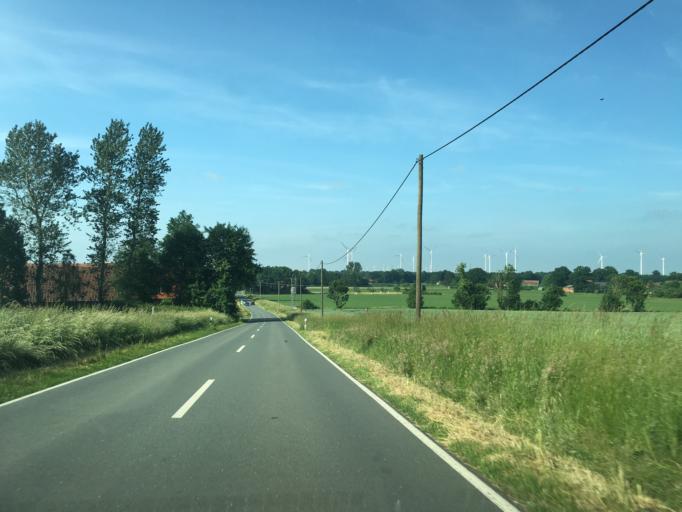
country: DE
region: North Rhine-Westphalia
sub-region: Regierungsbezirk Munster
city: Steinfurt
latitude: 52.1548
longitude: 7.3778
